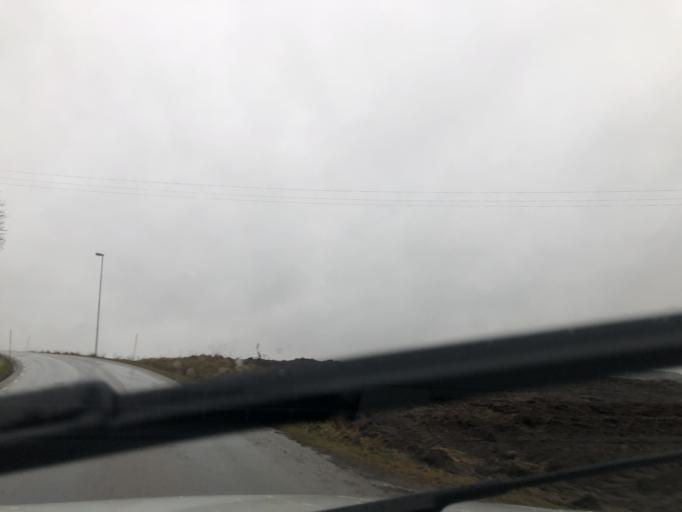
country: SE
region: Vaestra Goetaland
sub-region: Ulricehamns Kommun
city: Ulricehamn
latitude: 57.8606
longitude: 13.5523
